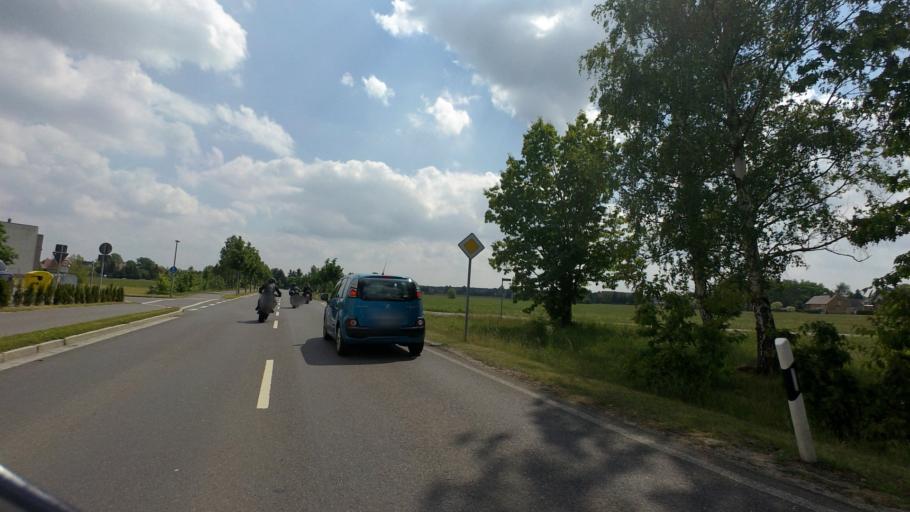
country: DE
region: Saxony
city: Weisskeissel
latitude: 51.4979
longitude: 14.7155
